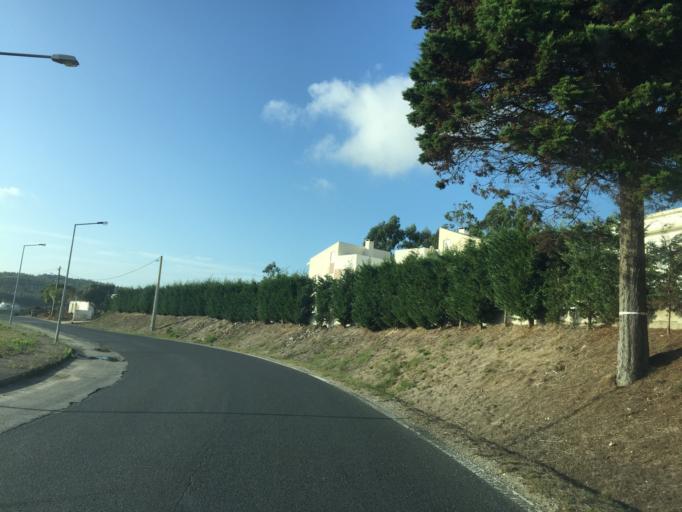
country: PT
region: Lisbon
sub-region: Torres Vedras
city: Torres Vedras
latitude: 39.1250
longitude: -9.2612
